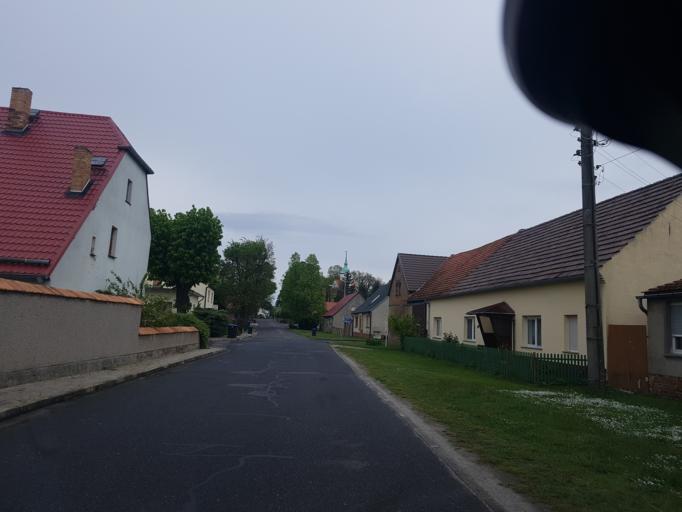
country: DE
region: Brandenburg
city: Sallgast
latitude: 51.6091
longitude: 13.8579
